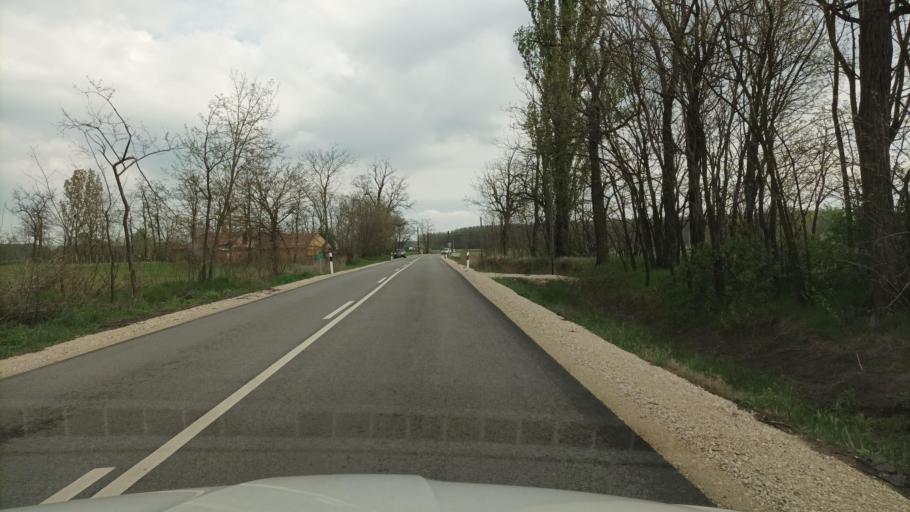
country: HU
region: Pest
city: Kocser
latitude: 47.0109
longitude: 19.8858
